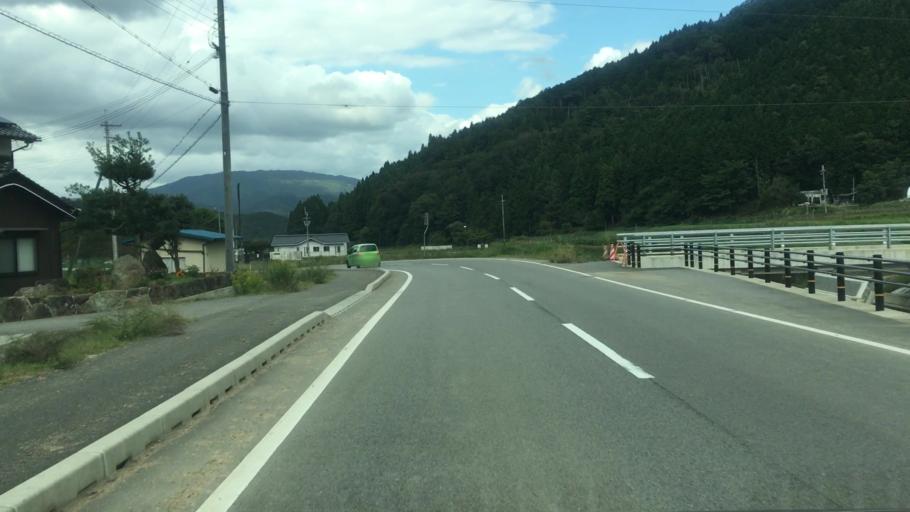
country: JP
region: Hyogo
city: Toyooka
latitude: 35.4400
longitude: 134.7324
